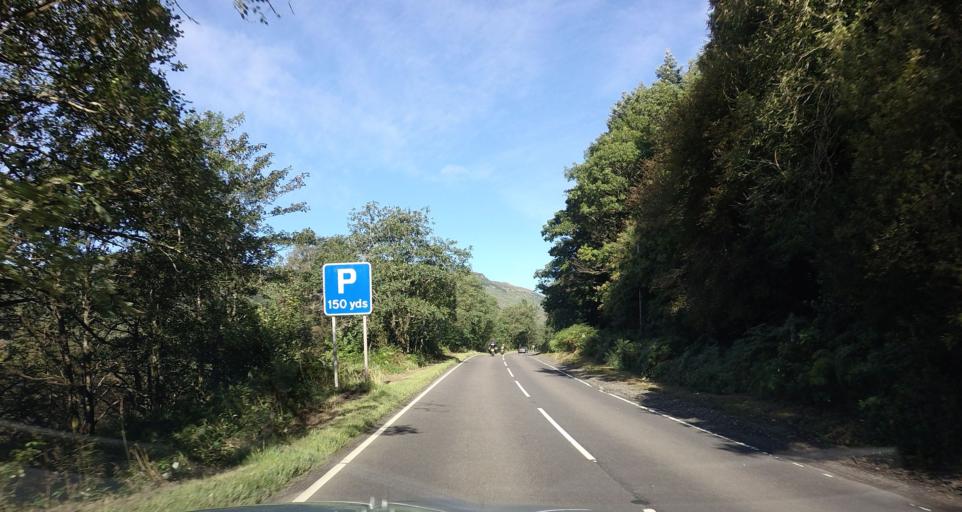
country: GB
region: Scotland
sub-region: Stirling
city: Callander
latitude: 56.3059
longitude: -4.3215
